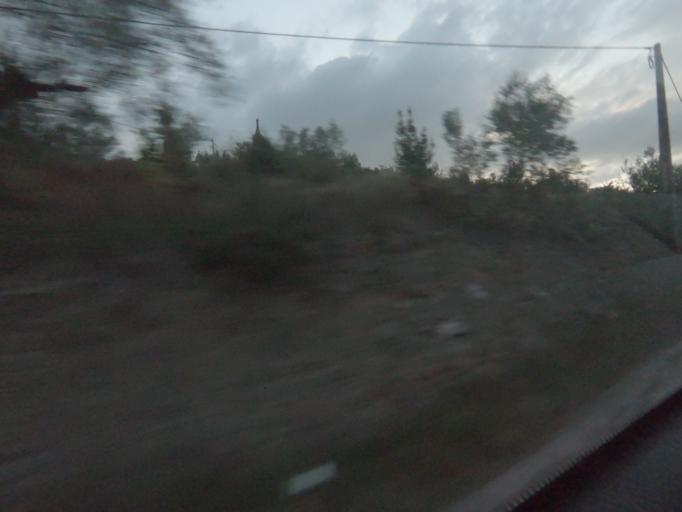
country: PT
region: Viseu
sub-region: Armamar
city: Armamar
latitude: 41.1149
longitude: -7.7169
